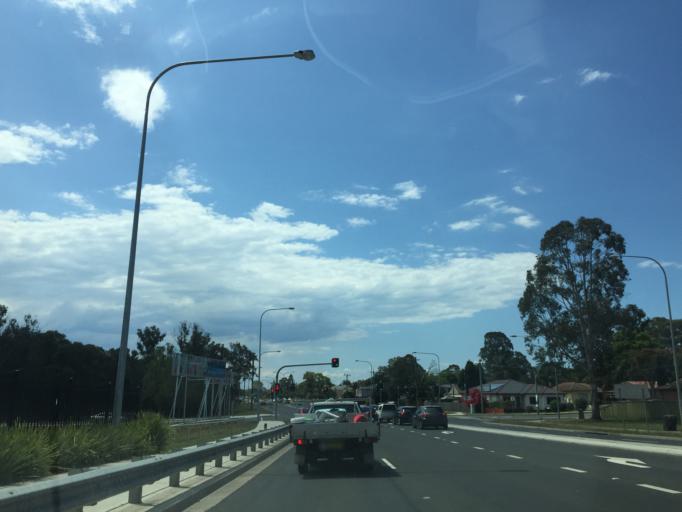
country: AU
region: New South Wales
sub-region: Blacktown
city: Doonside
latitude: -33.7636
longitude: 150.8628
